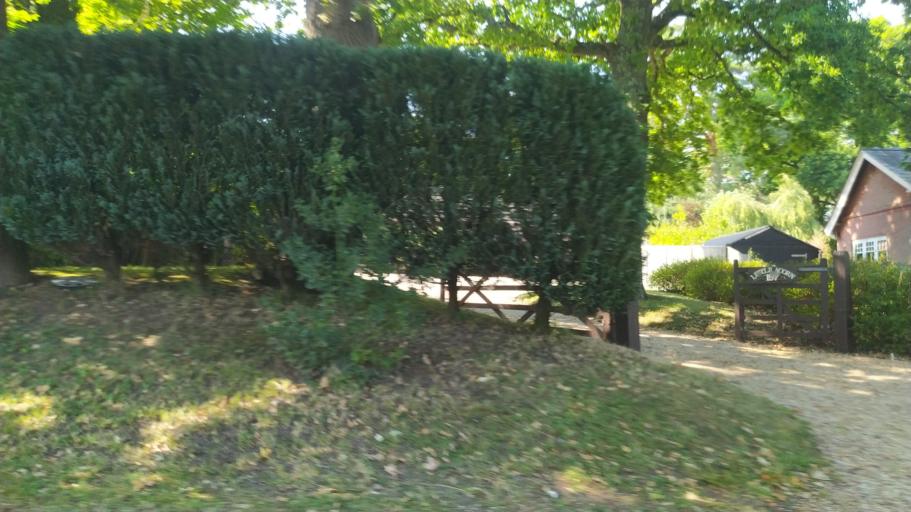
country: GB
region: England
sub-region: Hampshire
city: Cadnam
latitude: 50.9042
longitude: -1.5423
